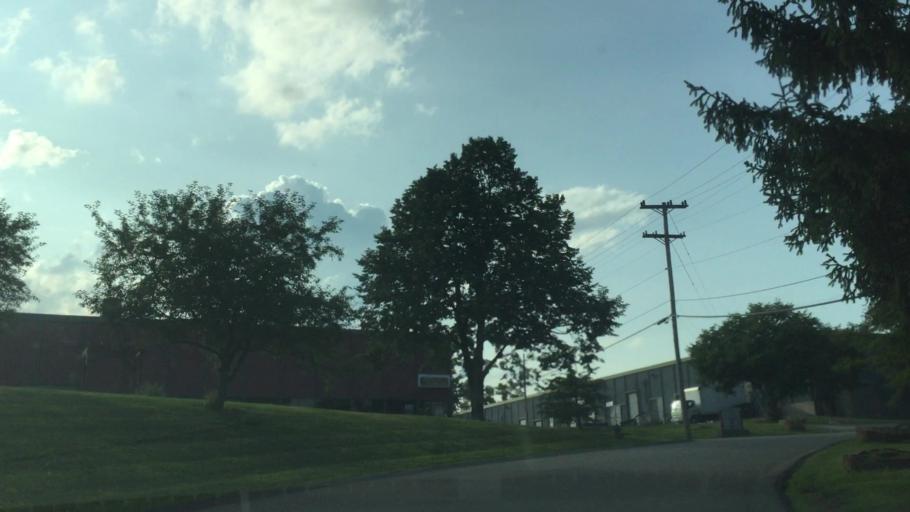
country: US
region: Pennsylvania
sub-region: Allegheny County
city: Rennerdale
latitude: 40.4325
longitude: -80.1315
